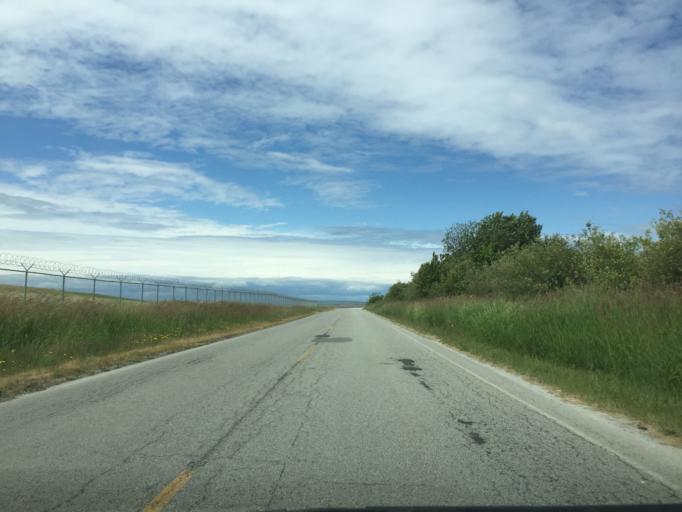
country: CA
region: British Columbia
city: Richmond
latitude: 49.2068
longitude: -123.1942
